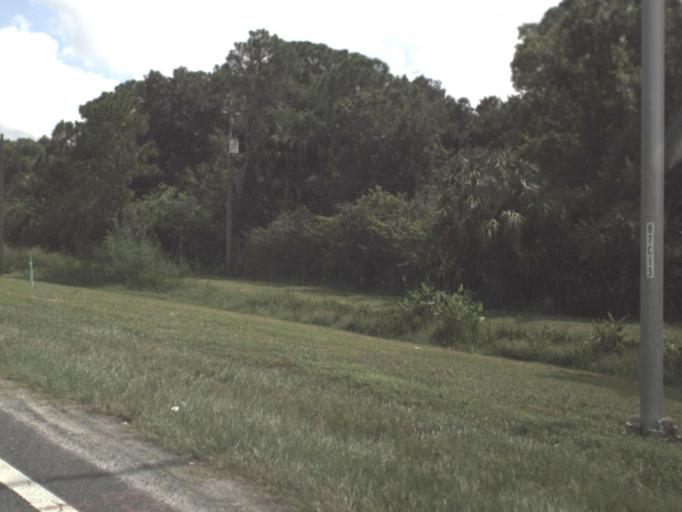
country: US
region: Florida
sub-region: Manatee County
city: Ellenton
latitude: 27.4917
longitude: -82.4776
